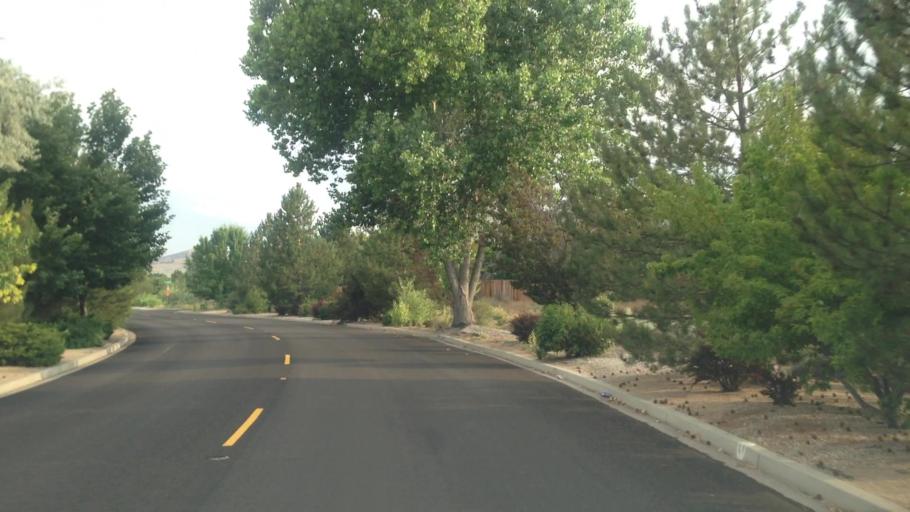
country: US
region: Nevada
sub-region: Washoe County
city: Lemmon Valley
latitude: 39.6304
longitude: -119.8755
